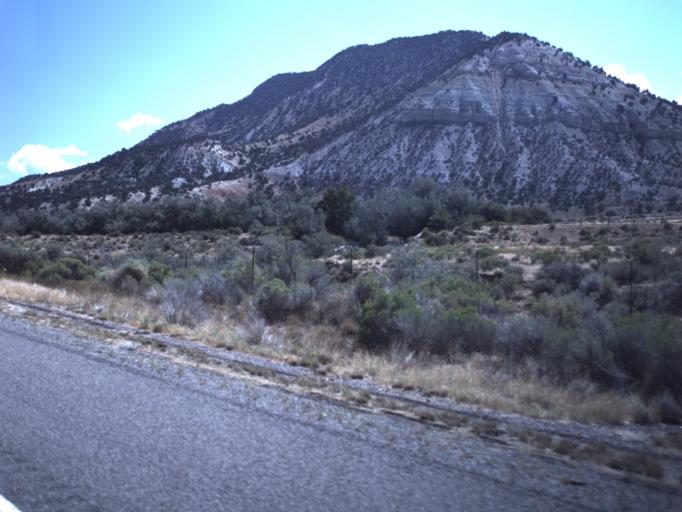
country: US
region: Utah
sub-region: Sevier County
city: Salina
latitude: 38.9316
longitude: -111.8160
